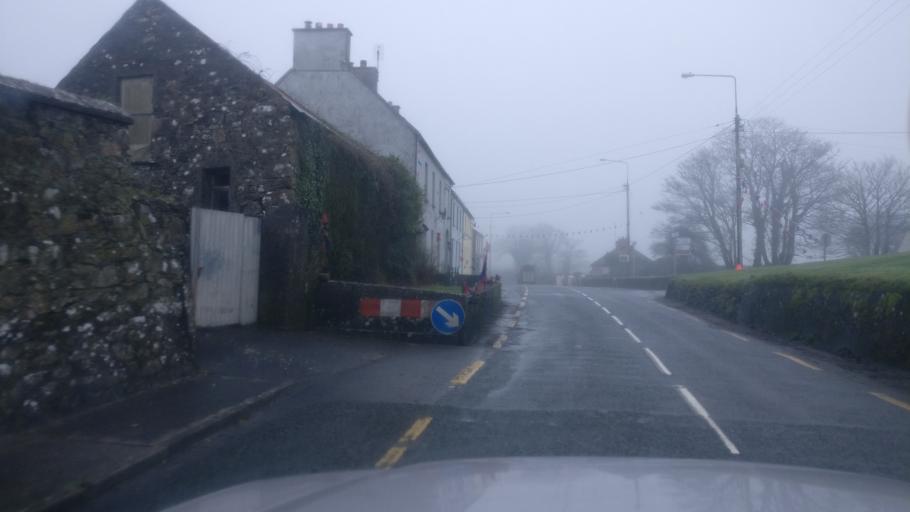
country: IE
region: Connaught
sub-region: County Galway
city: Loughrea
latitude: 53.1781
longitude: -8.6535
